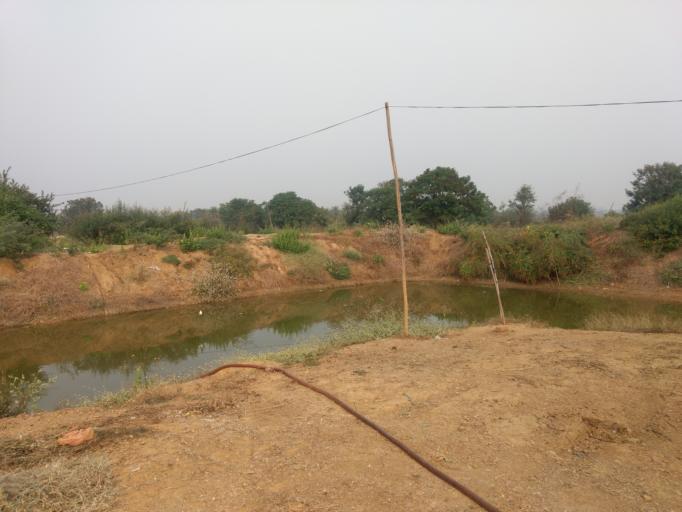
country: IN
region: Maharashtra
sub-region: Chandrapur
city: Mul
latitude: 19.9077
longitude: 79.9249
